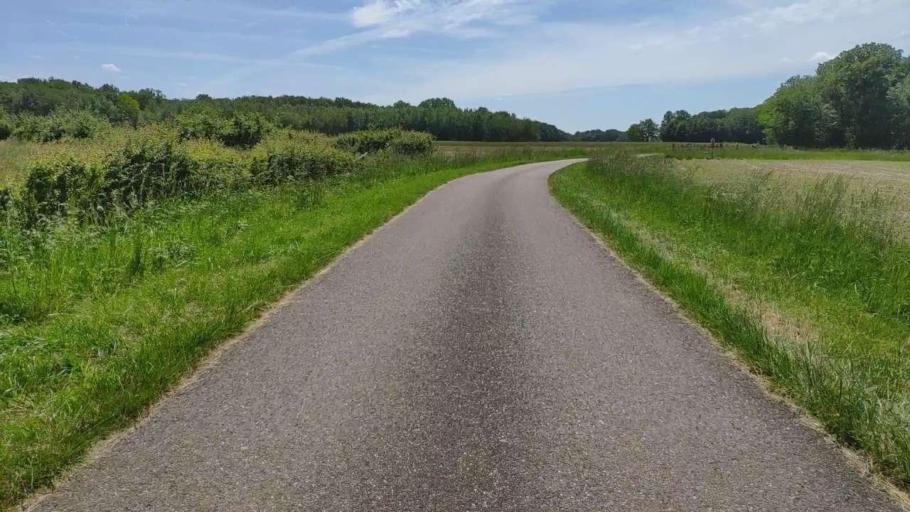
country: FR
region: Franche-Comte
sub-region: Departement du Jura
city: Bletterans
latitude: 46.7793
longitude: 5.3769
